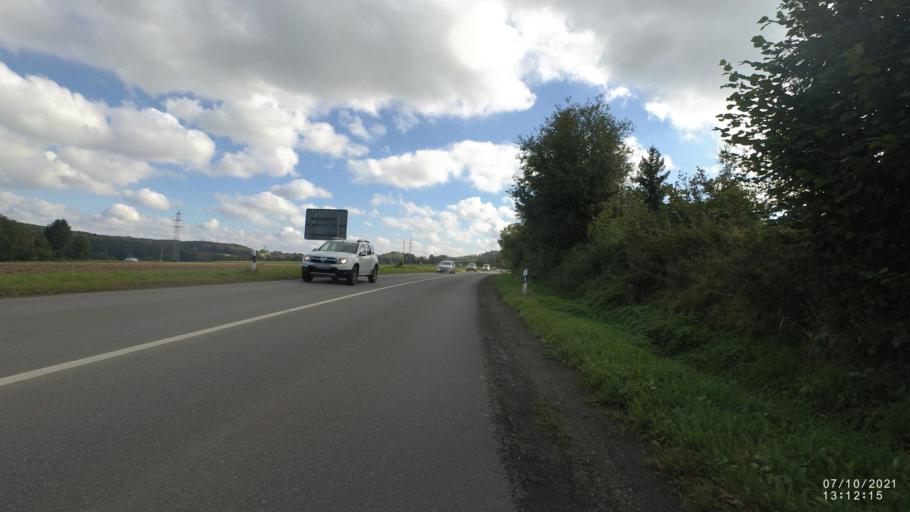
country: DE
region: North Rhine-Westphalia
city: Iserlohn
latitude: 51.4048
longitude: 7.7226
